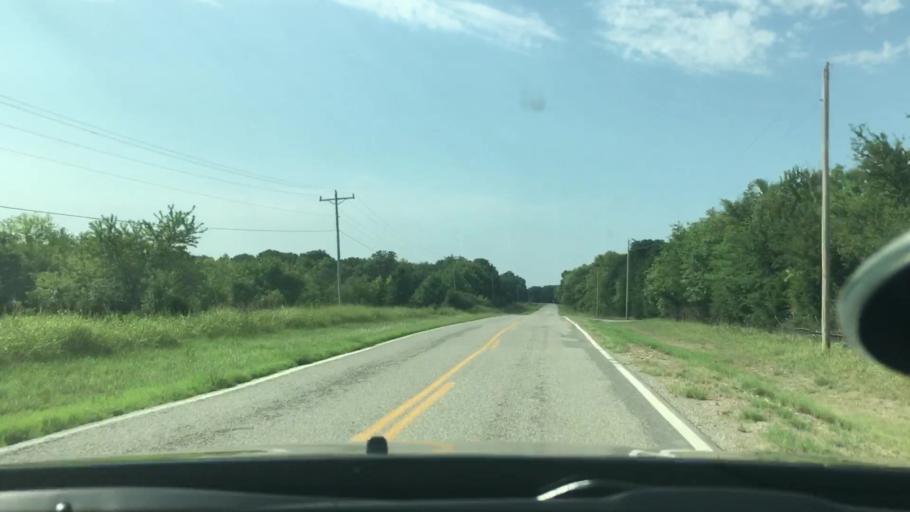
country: US
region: Oklahoma
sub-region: Johnston County
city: Tishomingo
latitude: 34.1751
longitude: -96.5838
